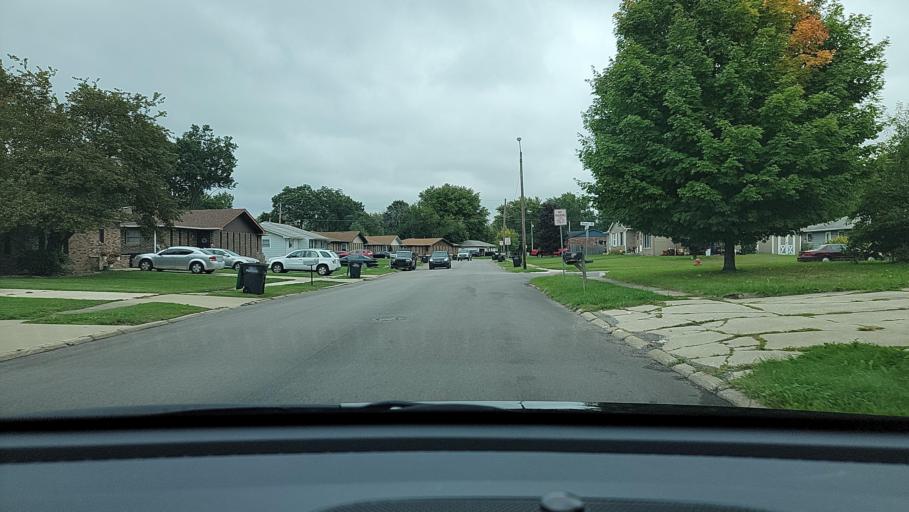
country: US
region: Indiana
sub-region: Lake County
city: Lake Station
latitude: 41.5573
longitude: -87.2093
